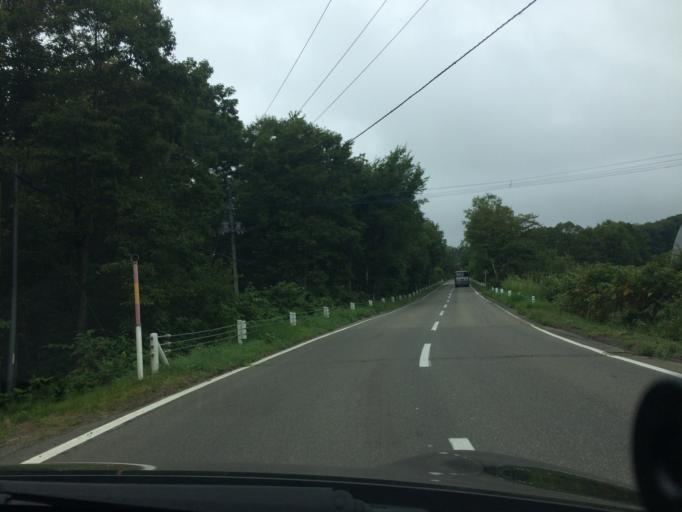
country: JP
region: Hokkaido
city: Otofuke
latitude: 42.9859
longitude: 143.0830
